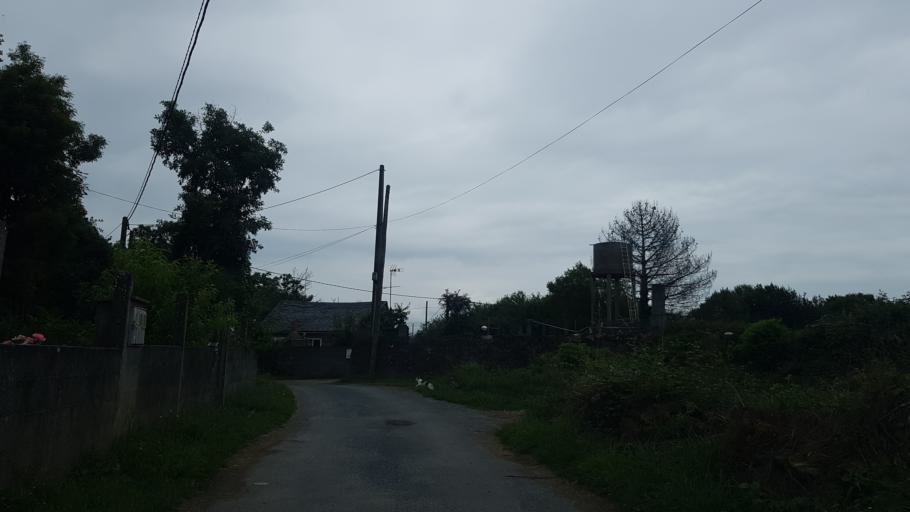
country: ES
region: Galicia
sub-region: Provincia de Lugo
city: Lugo
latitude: 43.0308
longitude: -7.5406
